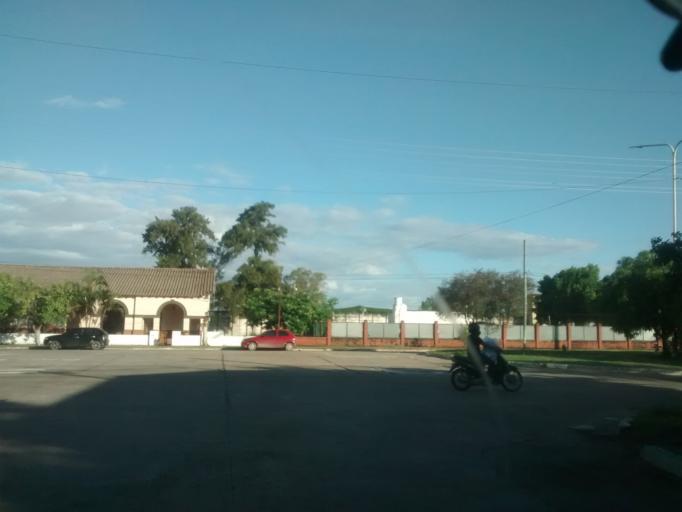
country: AR
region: Chaco
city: Resistencia
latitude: -27.4678
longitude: -58.9913
